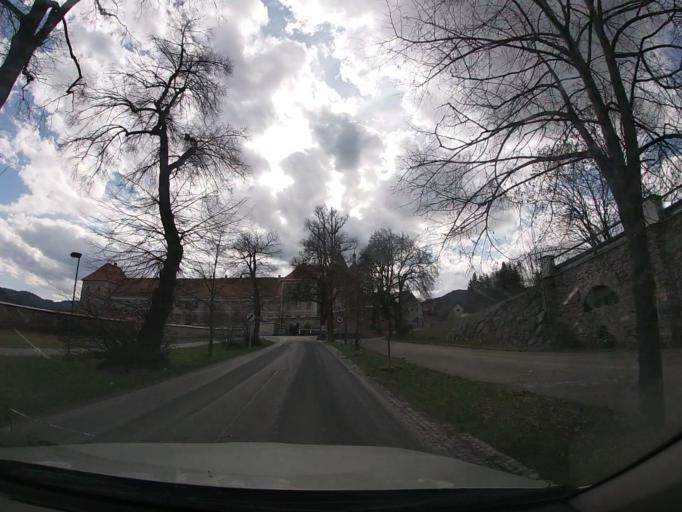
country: AT
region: Styria
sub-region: Politischer Bezirk Murau
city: Sankt Lambrecht
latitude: 47.0726
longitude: 14.3029
